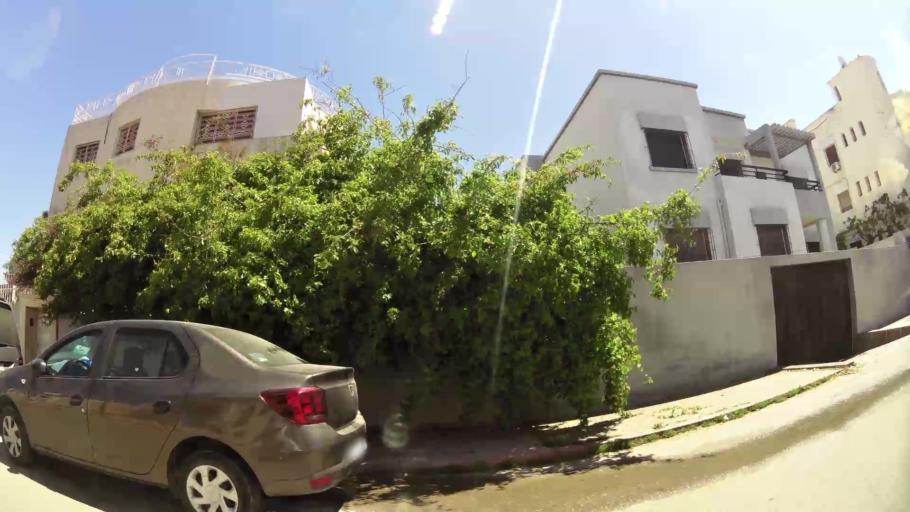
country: MA
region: Meknes-Tafilalet
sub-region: Meknes
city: Meknes
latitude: 33.8909
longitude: -5.5466
